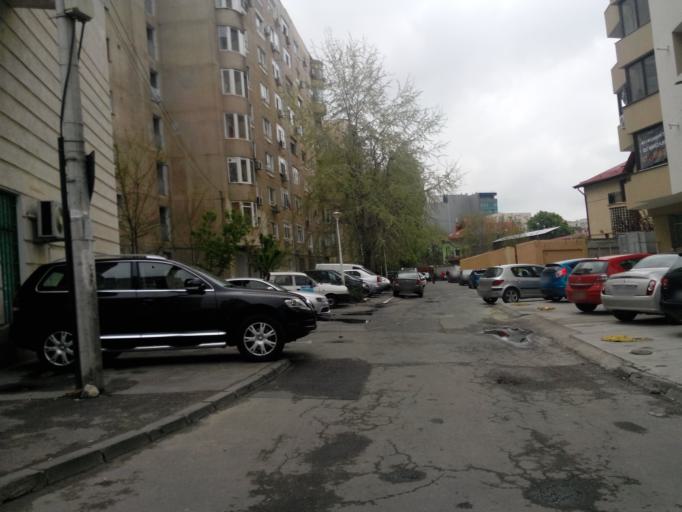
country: RO
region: Bucuresti
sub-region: Municipiul Bucuresti
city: Bucharest
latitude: 44.4319
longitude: 26.1259
